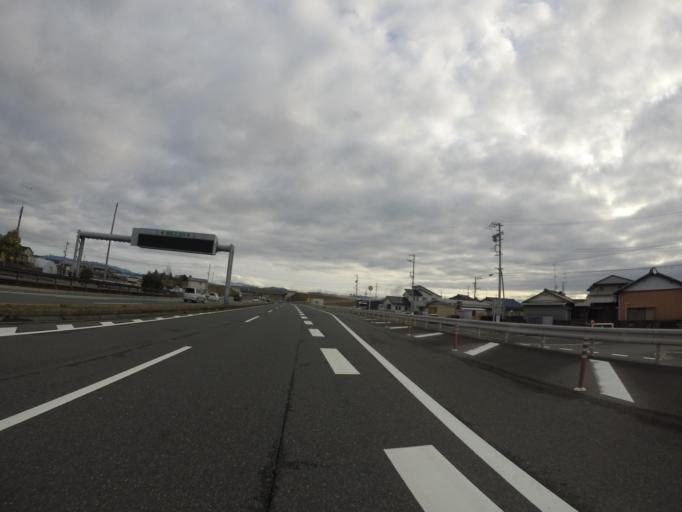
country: JP
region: Shizuoka
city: Hamakita
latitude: 34.8274
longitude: 137.8105
